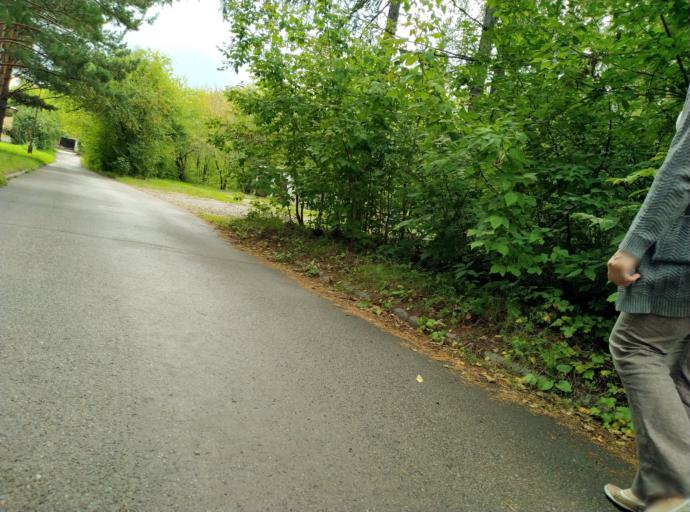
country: RU
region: Krasnoyarskiy
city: Krasnoyarsk
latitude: 55.9894
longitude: 92.7610
